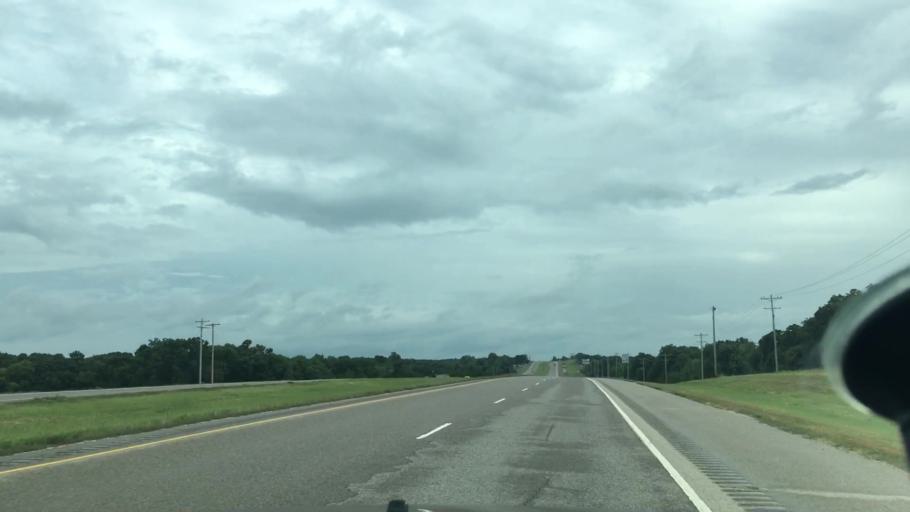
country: US
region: Oklahoma
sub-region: Seminole County
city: Seminole
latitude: 35.3326
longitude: -96.6717
